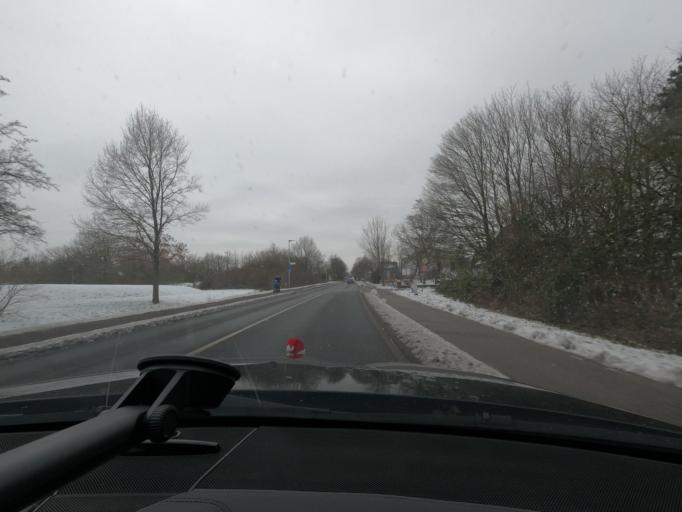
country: DE
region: Schleswig-Holstein
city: Jarplund-Weding
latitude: 54.7592
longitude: 9.4079
